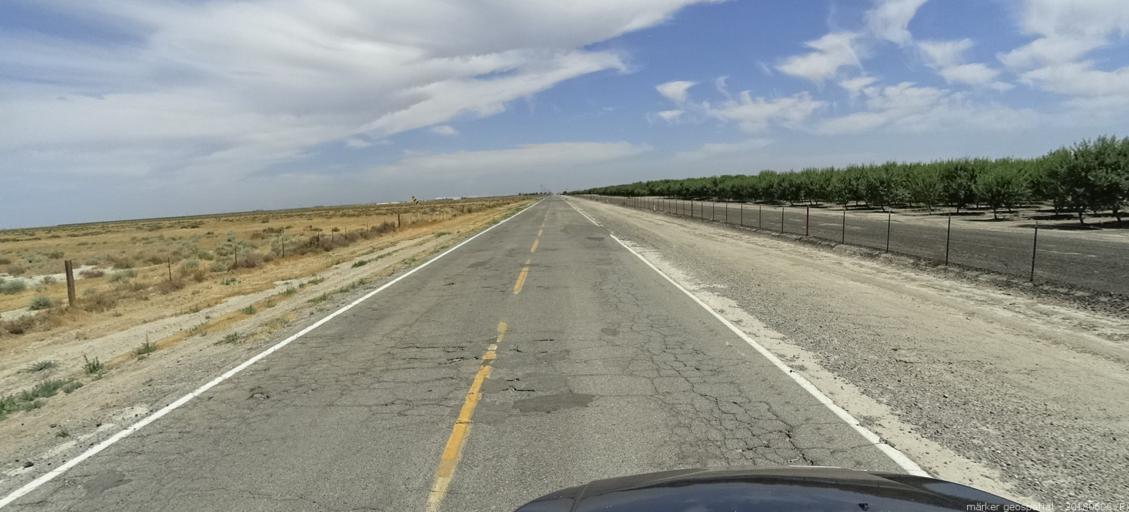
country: US
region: California
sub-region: Fresno County
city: Firebaugh
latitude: 36.9112
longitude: -120.3820
